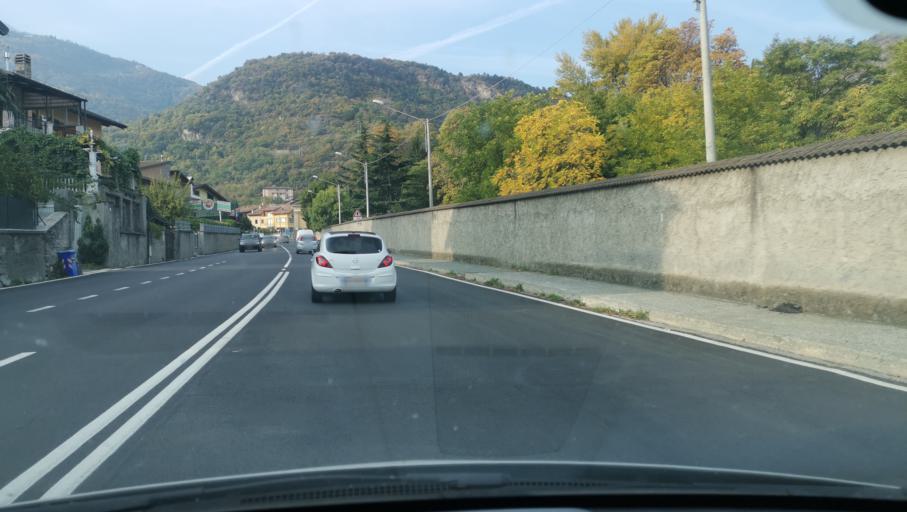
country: IT
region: Piedmont
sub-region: Provincia di Torino
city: Susa
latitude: 45.1331
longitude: 7.0468
